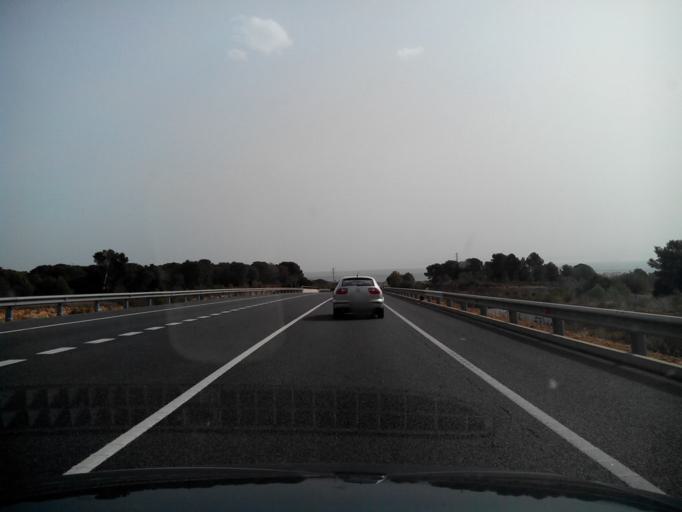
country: ES
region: Catalonia
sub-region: Provincia de Tarragona
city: Torredembarra
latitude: 41.1609
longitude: 1.4148
